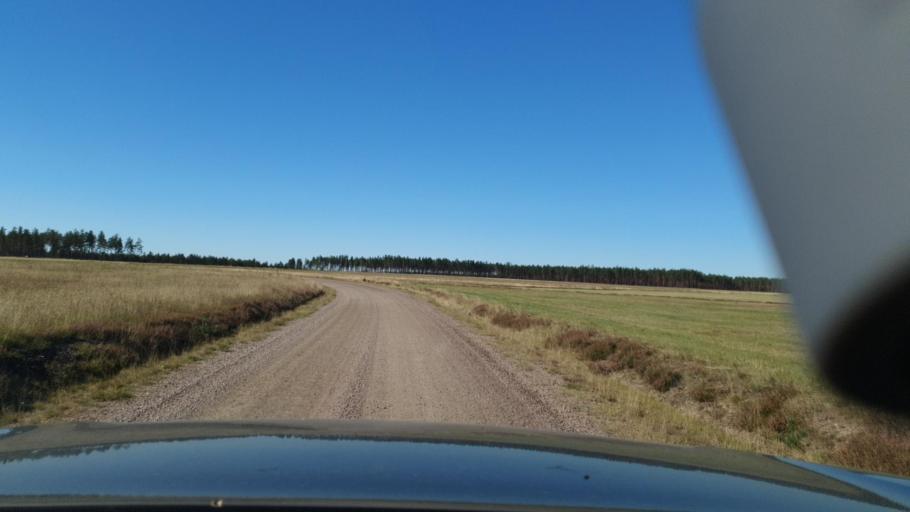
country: SE
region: Vaermland
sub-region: Karlstads Kommun
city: Molkom
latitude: 59.6084
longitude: 13.9205
